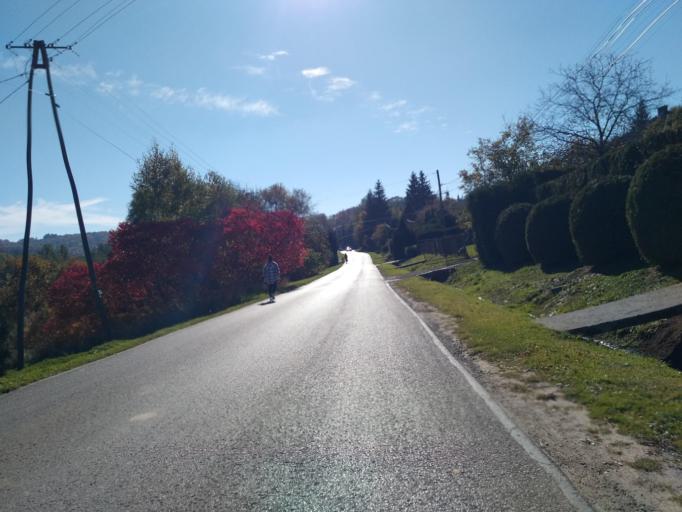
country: PL
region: Subcarpathian Voivodeship
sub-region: Powiat ropczycko-sedziszowski
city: Iwierzyce
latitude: 49.9885
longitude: 21.7268
